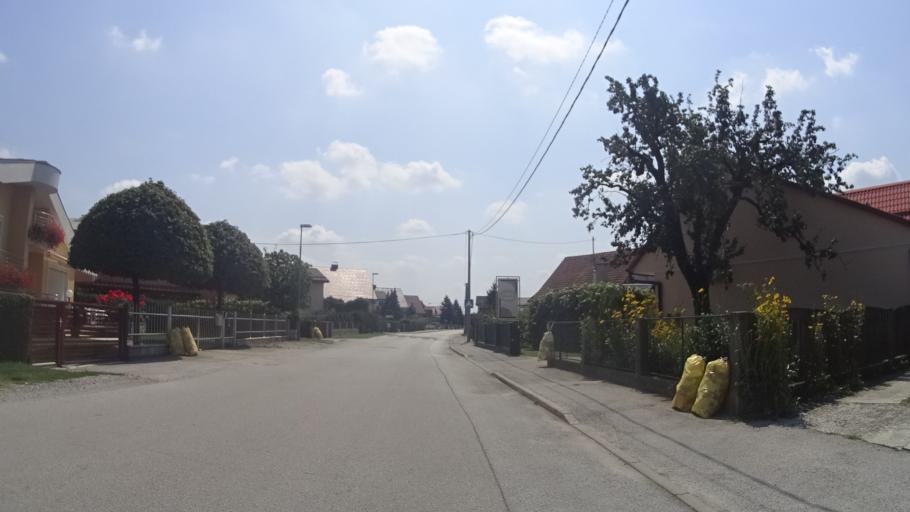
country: SI
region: Miklavz na Dravskem Polju
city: Miklavz na Dravskem Polju
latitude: 46.5041
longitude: 15.7025
